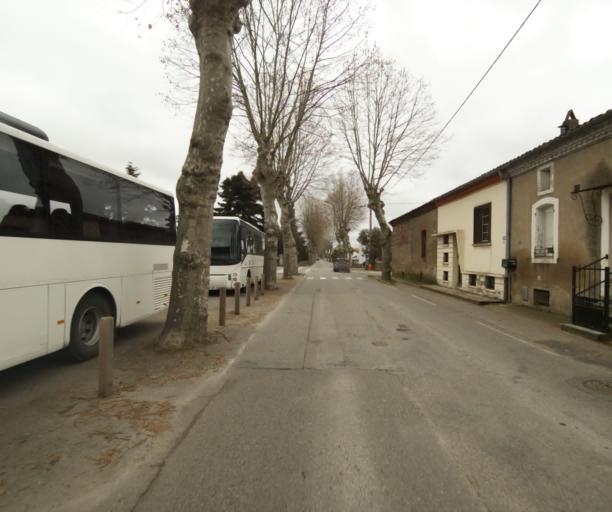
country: FR
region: Midi-Pyrenees
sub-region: Departement de l'Ariege
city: Pamiers
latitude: 43.1156
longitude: 1.6234
